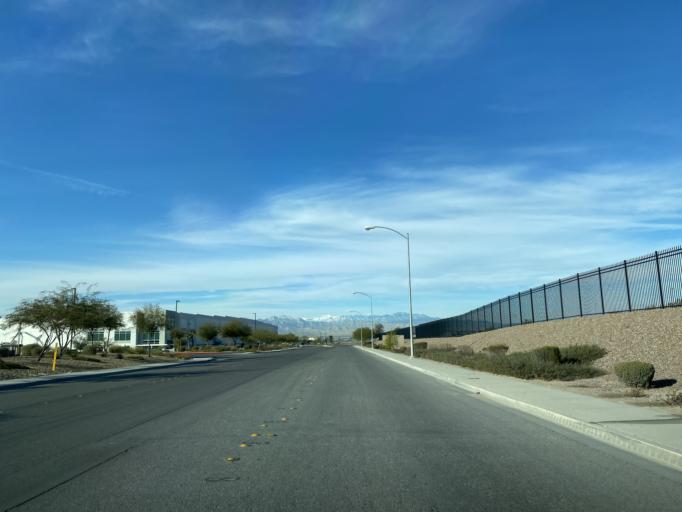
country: US
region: Nevada
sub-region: Clark County
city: Nellis Air Force Base
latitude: 36.2623
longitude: -115.0456
